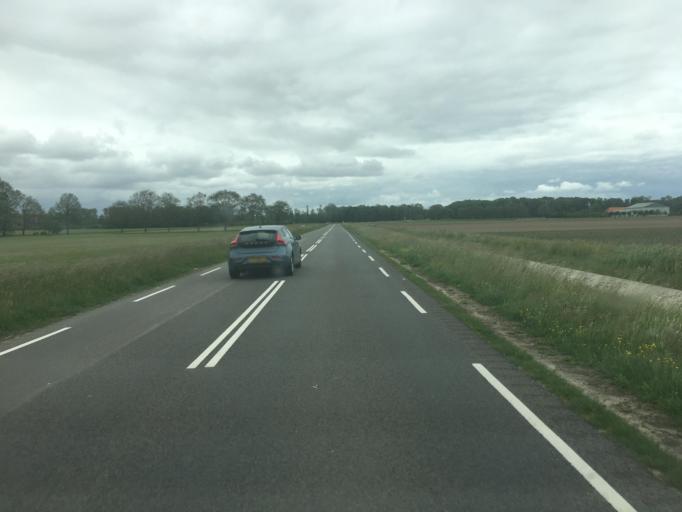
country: NL
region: Flevoland
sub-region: Gemeente Noordoostpolder
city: Ens
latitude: 52.6390
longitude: 5.7595
